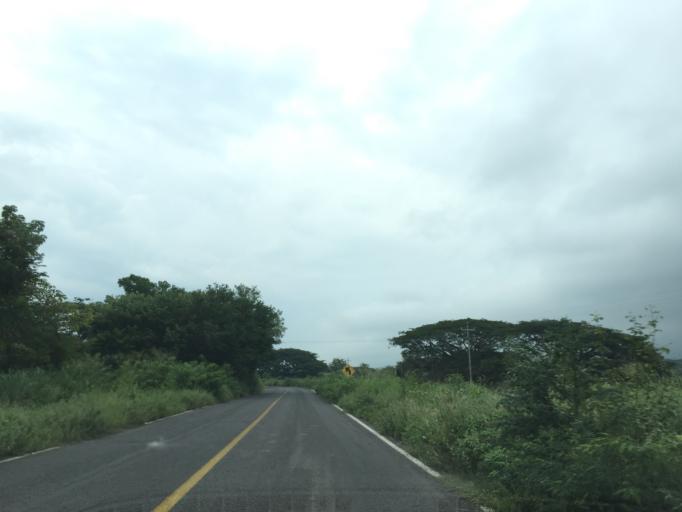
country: MX
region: Colima
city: Comala
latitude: 19.3595
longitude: -103.7944
